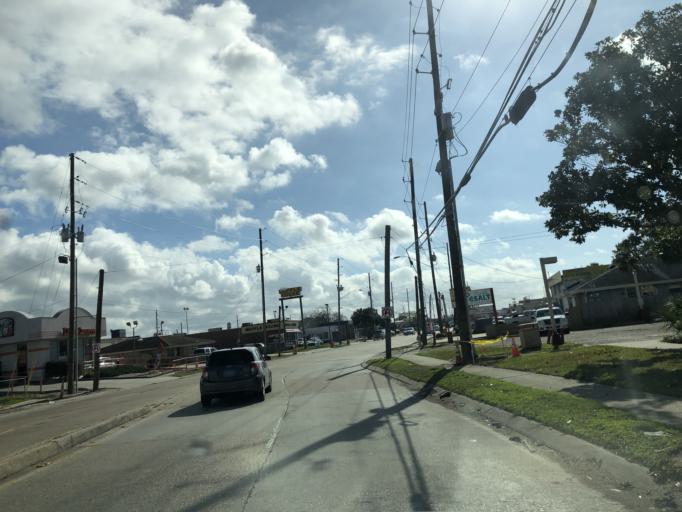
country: US
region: Louisiana
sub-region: Jefferson Parish
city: Kenner
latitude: 30.0046
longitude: -90.2207
